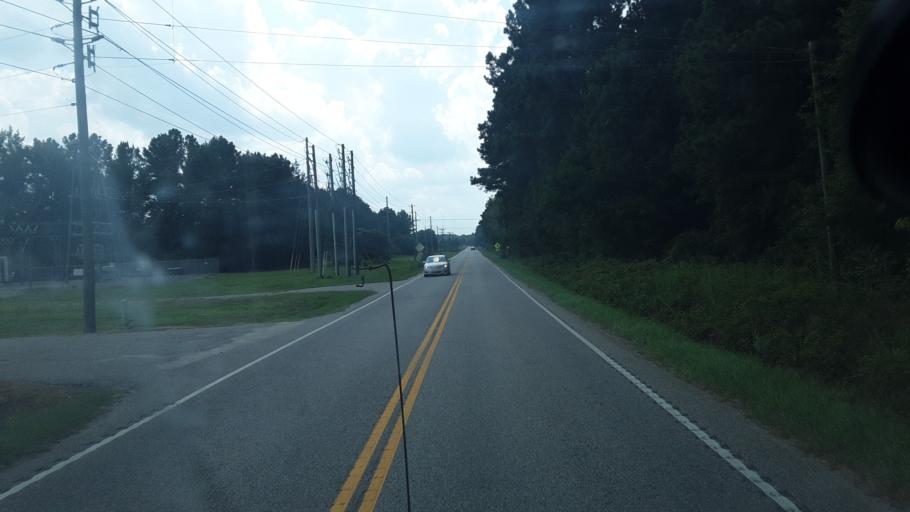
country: US
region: South Carolina
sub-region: Sumter County
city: Sumter
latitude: 33.9670
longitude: -80.3641
